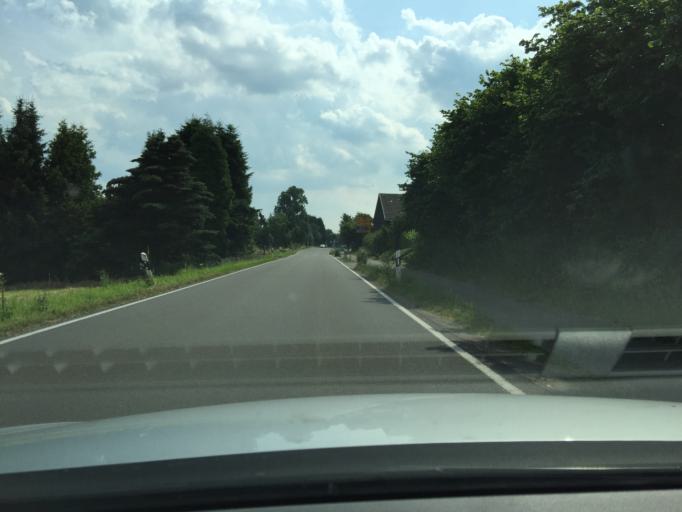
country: DE
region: North Rhine-Westphalia
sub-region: Regierungsbezirk Dusseldorf
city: Velbert
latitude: 51.3549
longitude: 7.0904
